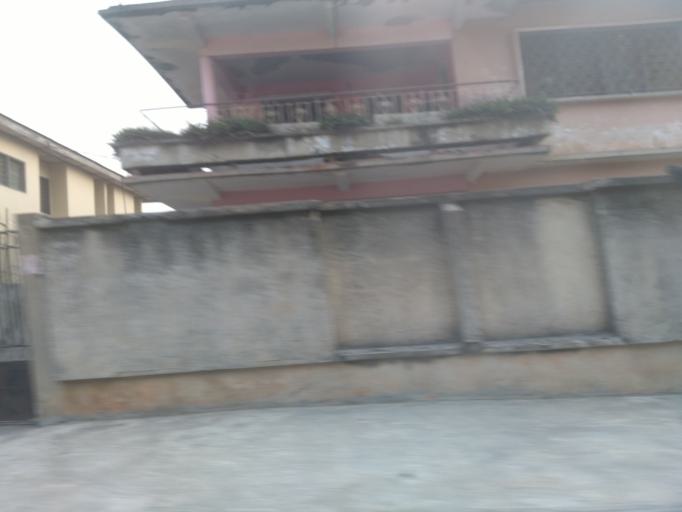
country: GH
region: Ashanti
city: Tafo
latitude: 6.7096
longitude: -1.6107
